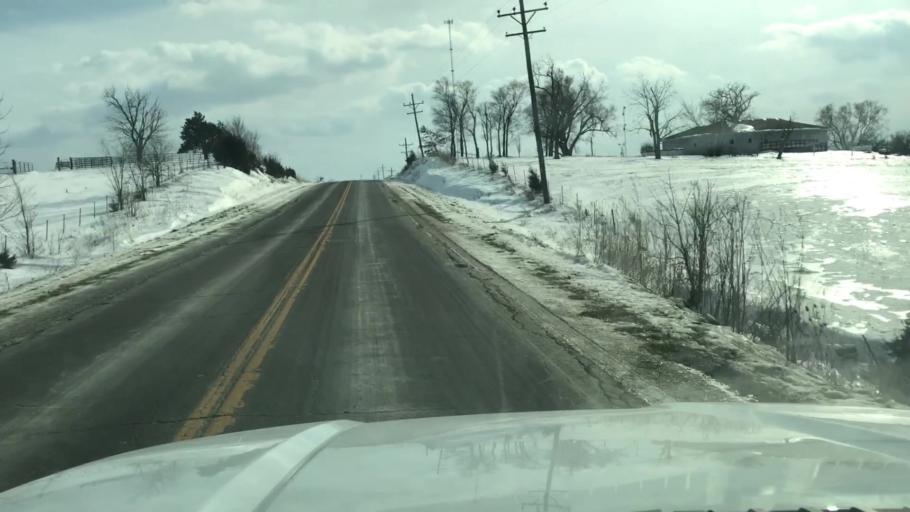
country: US
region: Missouri
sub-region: Gentry County
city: Stanberry
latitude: 40.3752
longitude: -94.6472
